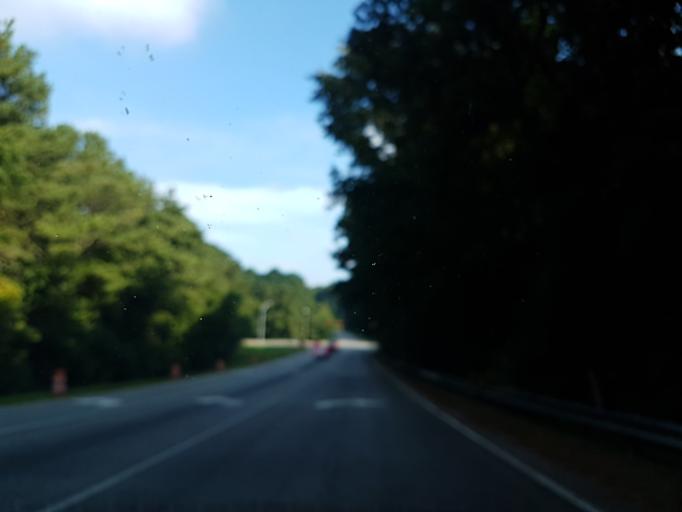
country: US
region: Georgia
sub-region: Cobb County
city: Marietta
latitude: 33.9607
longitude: -84.5179
